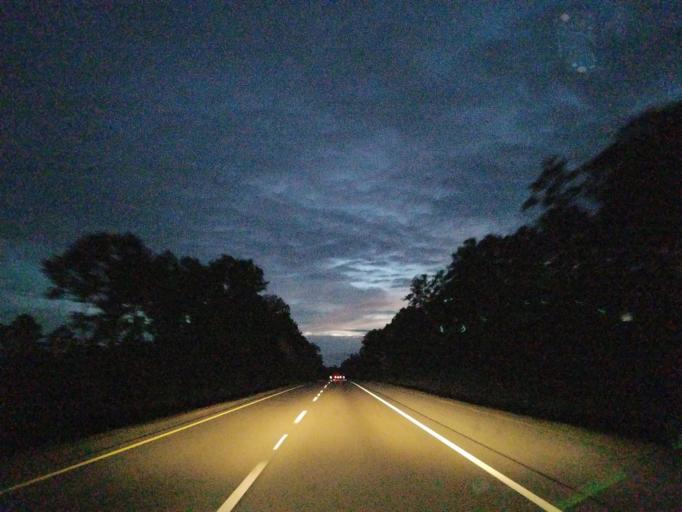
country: US
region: Mississippi
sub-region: Jones County
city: Laurel
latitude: 31.7344
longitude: -89.0938
